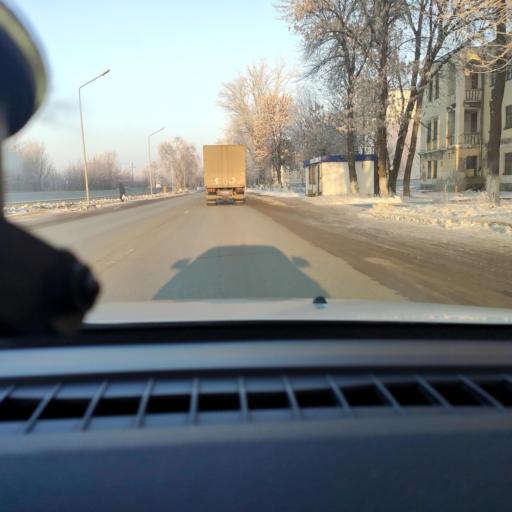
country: RU
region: Samara
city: Chapayevsk
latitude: 52.9716
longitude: 49.6995
